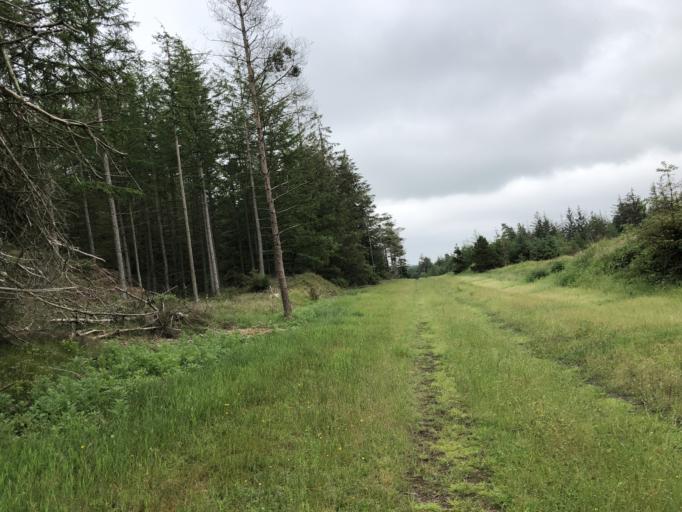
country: DK
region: Central Jutland
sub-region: Holstebro Kommune
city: Ulfborg
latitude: 56.2519
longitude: 8.3592
